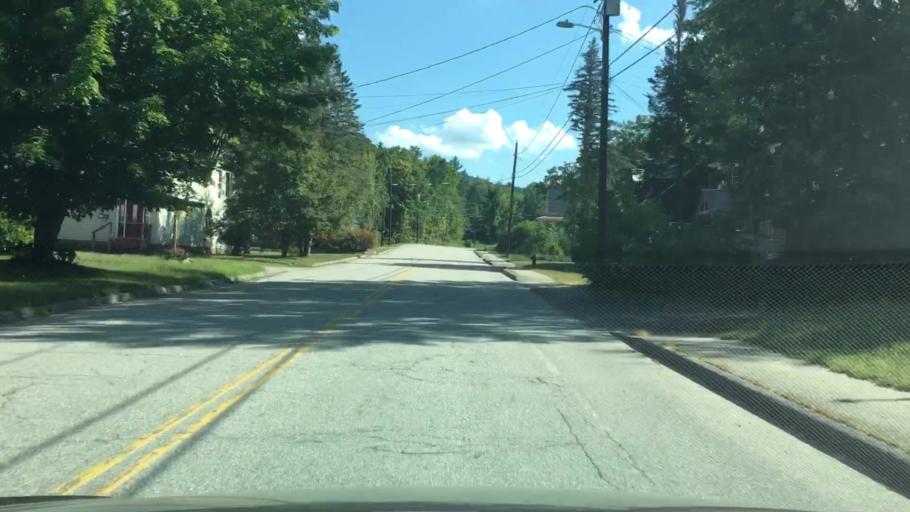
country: US
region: New Hampshire
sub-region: Carroll County
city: North Conway
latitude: 44.0731
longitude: -71.2831
